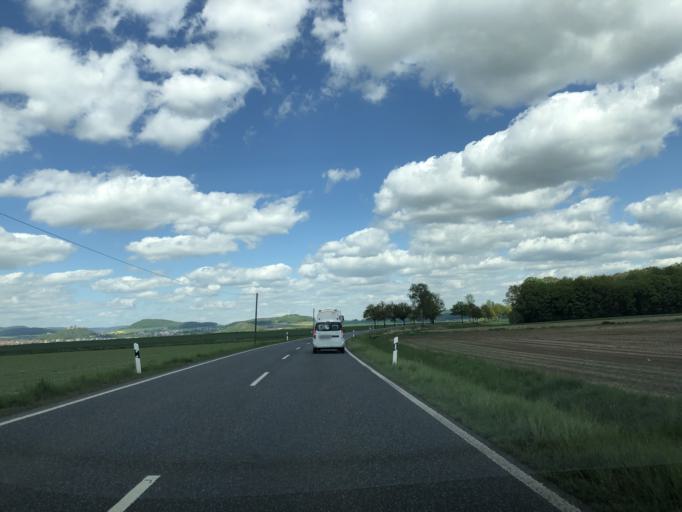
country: DE
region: Hesse
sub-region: Regierungsbezirk Kassel
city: Wabern
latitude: 51.1359
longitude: 9.3682
